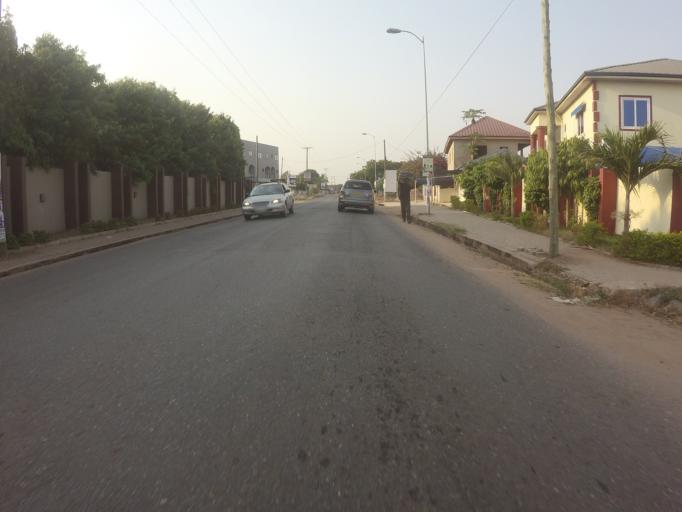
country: GH
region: Greater Accra
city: Nungua
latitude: 5.6194
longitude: -0.0545
